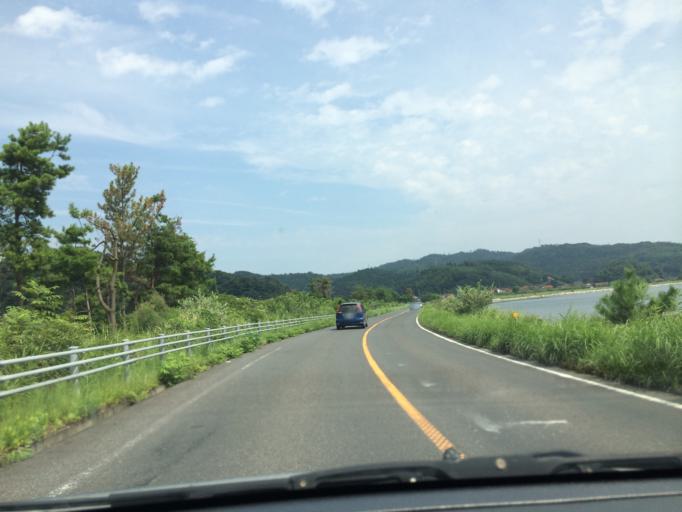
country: JP
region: Shimane
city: Sakaiminato
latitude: 35.5359
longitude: 133.1543
